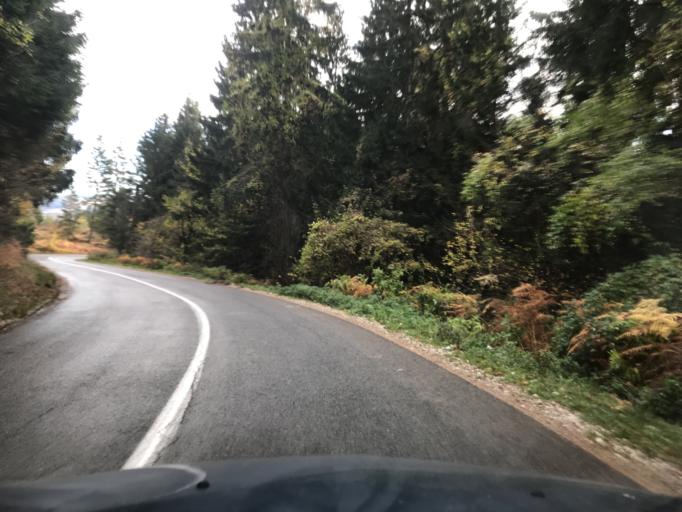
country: BA
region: Republika Srpska
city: Skender Vakuf
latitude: 44.5032
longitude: 17.3571
